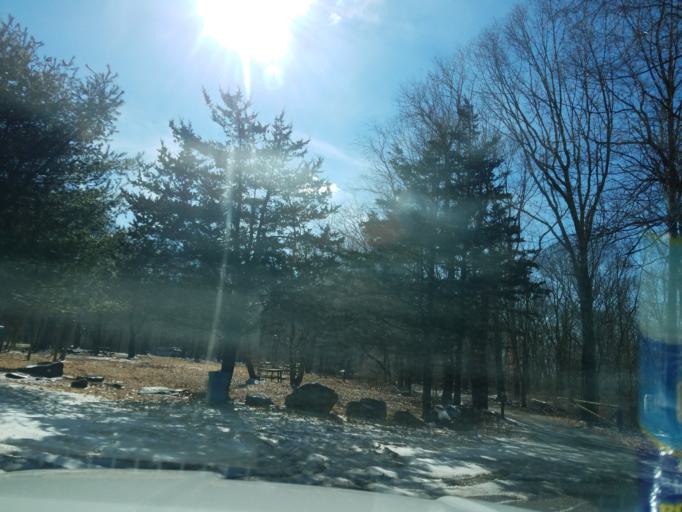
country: US
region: Connecticut
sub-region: New London County
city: Old Mystic
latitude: 41.4497
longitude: -71.9336
